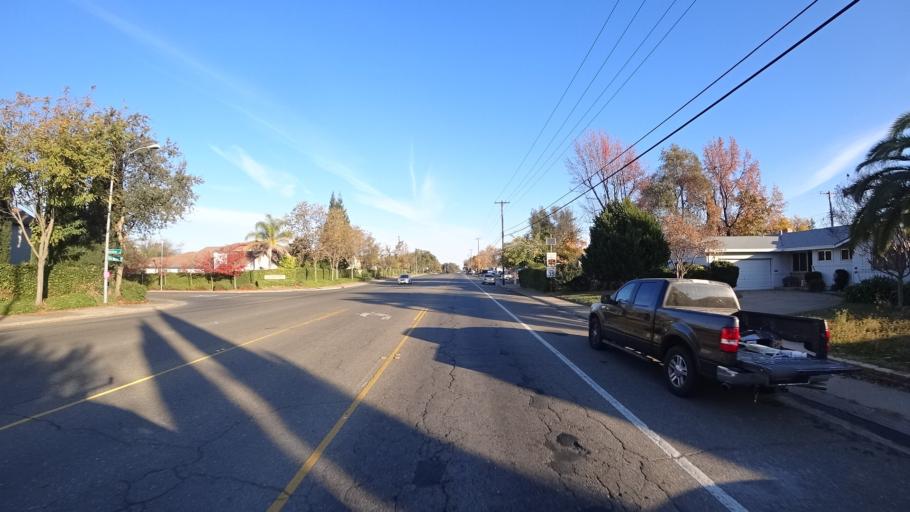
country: US
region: California
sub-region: Sacramento County
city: Antelope
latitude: 38.6900
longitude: -121.3087
